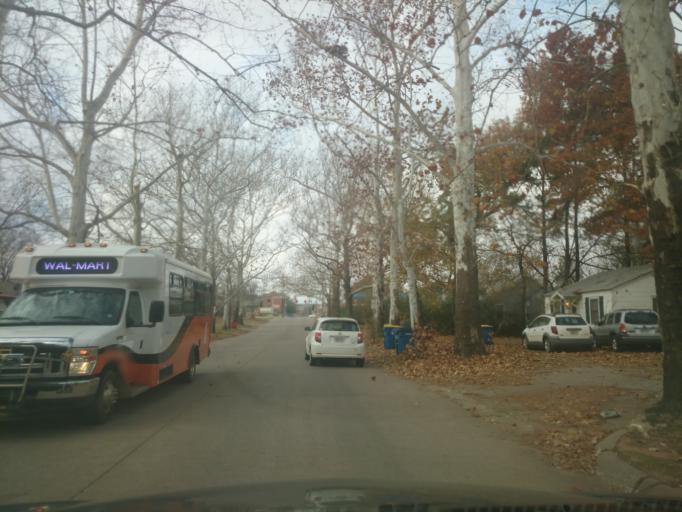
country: US
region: Oklahoma
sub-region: Payne County
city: Stillwater
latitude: 36.1238
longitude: -97.0567
